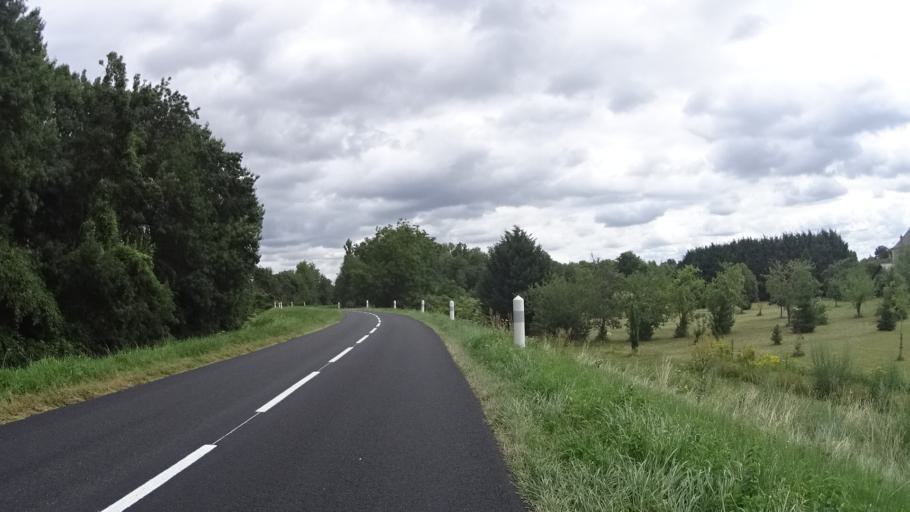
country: FR
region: Centre
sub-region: Departement d'Indre-et-Loire
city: Huismes
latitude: 47.2706
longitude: 0.3160
